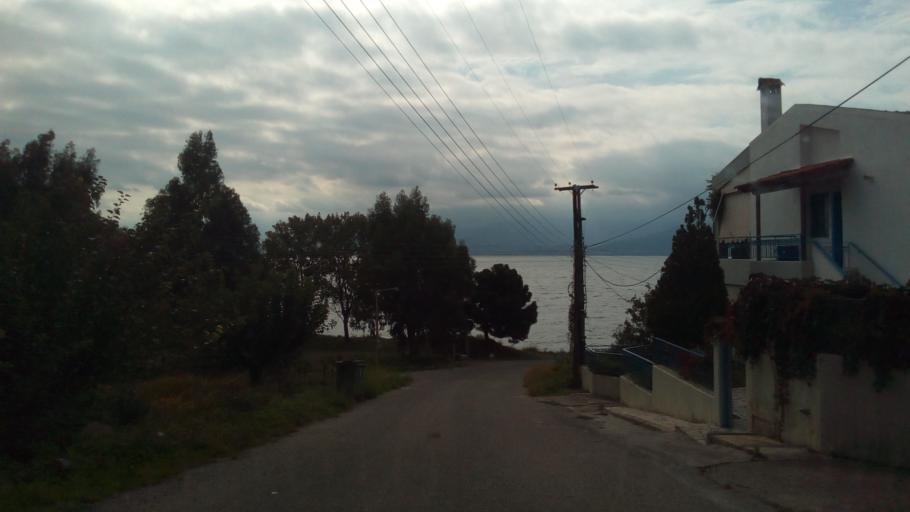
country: GR
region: West Greece
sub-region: Nomos Achaias
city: Kamarai
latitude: 38.3945
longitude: 22.0185
